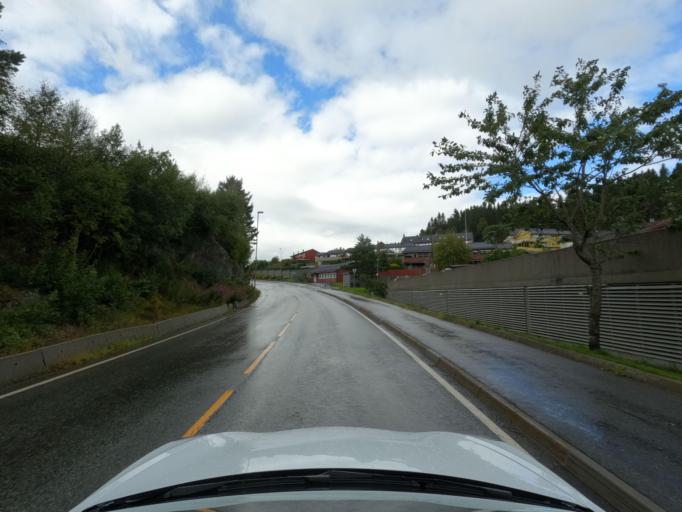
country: NO
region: Hordaland
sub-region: Bergen
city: Hylkje
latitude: 60.4621
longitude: 5.3713
